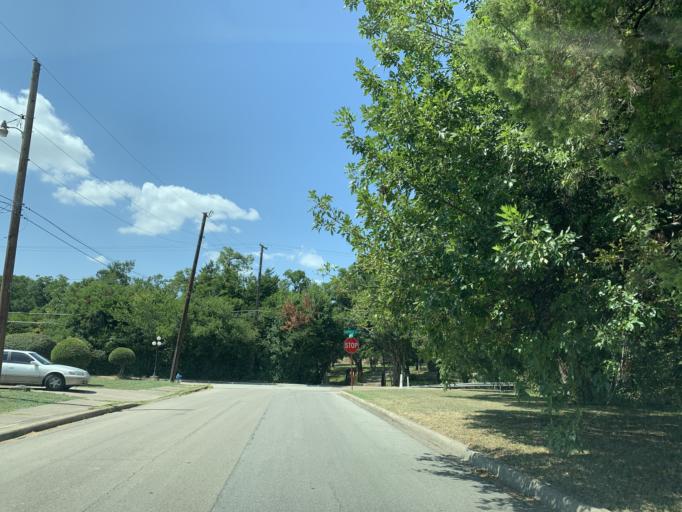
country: US
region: Texas
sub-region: Dallas County
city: Hutchins
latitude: 32.7103
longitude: -96.7657
